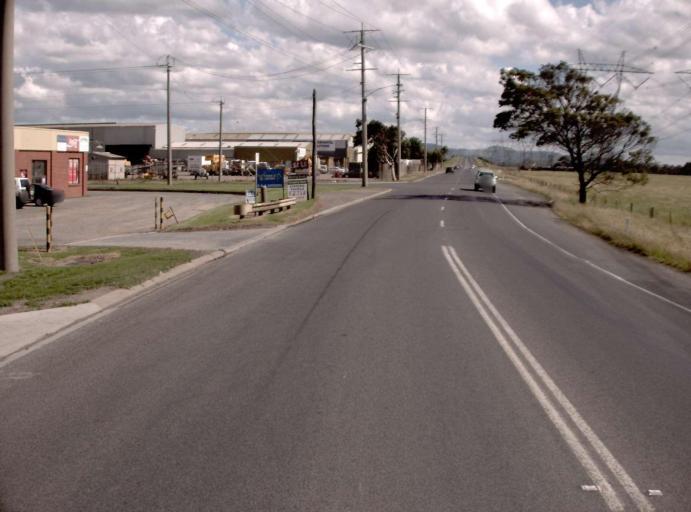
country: AU
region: Victoria
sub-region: Latrobe
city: Morwell
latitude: -38.2377
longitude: 146.4383
